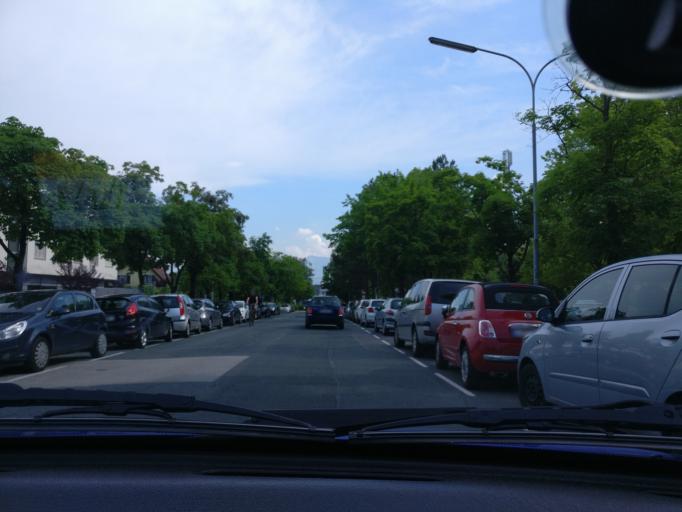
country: AT
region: Carinthia
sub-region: Klagenfurt am Woerthersee
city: Klagenfurt am Woerthersee
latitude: 46.6170
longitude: 14.2675
